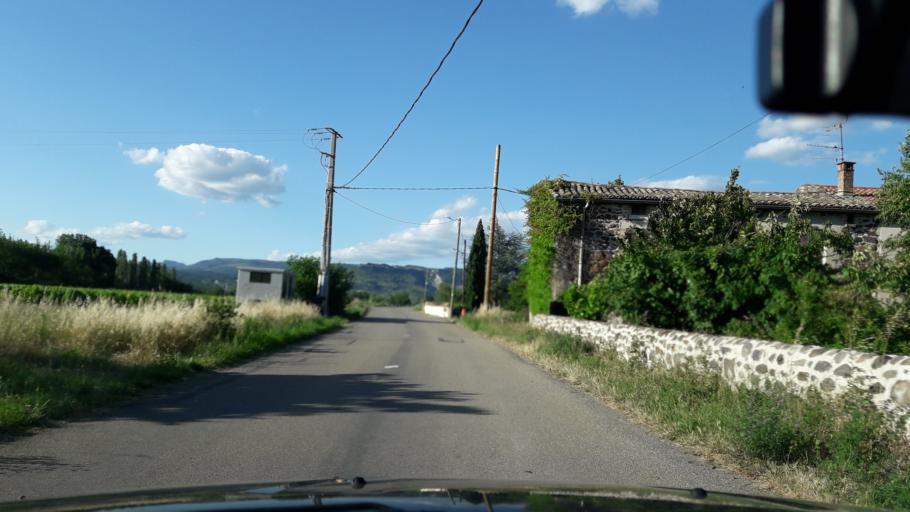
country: FR
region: Rhone-Alpes
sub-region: Departement de l'Ardeche
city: Lavilledieu
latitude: 44.5985
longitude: 4.4631
